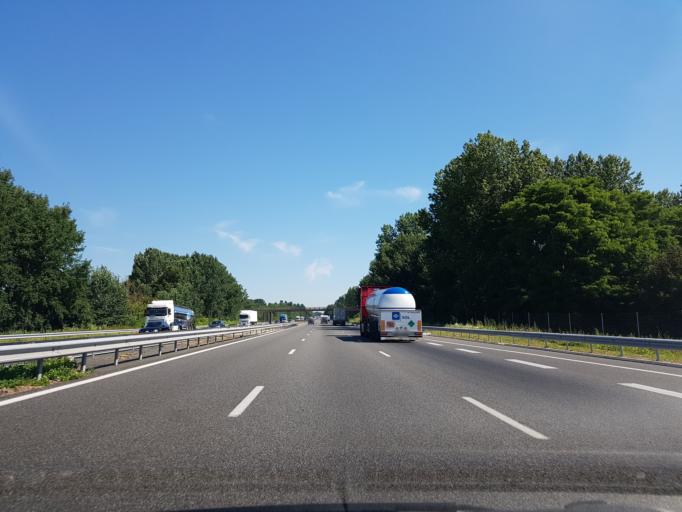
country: FR
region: Picardie
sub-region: Departement de l'Oise
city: Chevrieres
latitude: 49.3246
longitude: 2.6892
